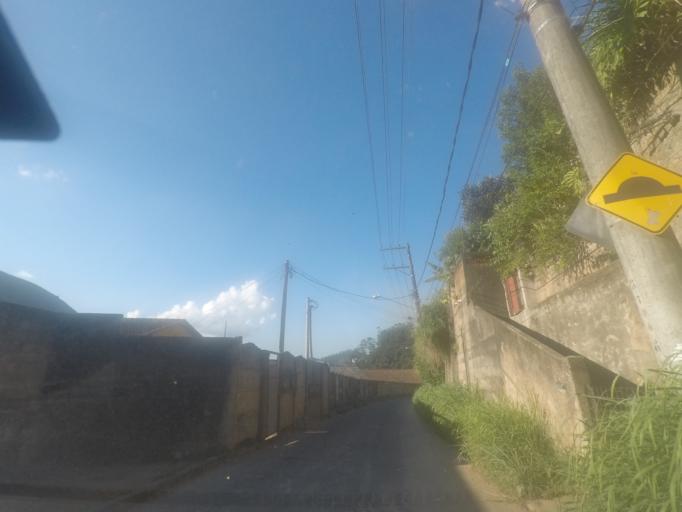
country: BR
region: Rio de Janeiro
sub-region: Petropolis
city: Petropolis
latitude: -22.4893
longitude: -43.1510
